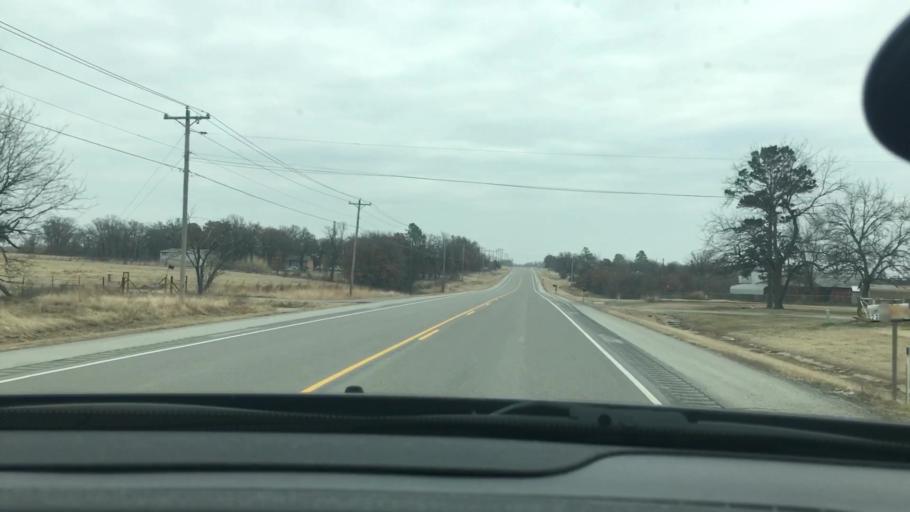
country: US
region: Oklahoma
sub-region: Carter County
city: Healdton
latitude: 34.4028
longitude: -97.5075
